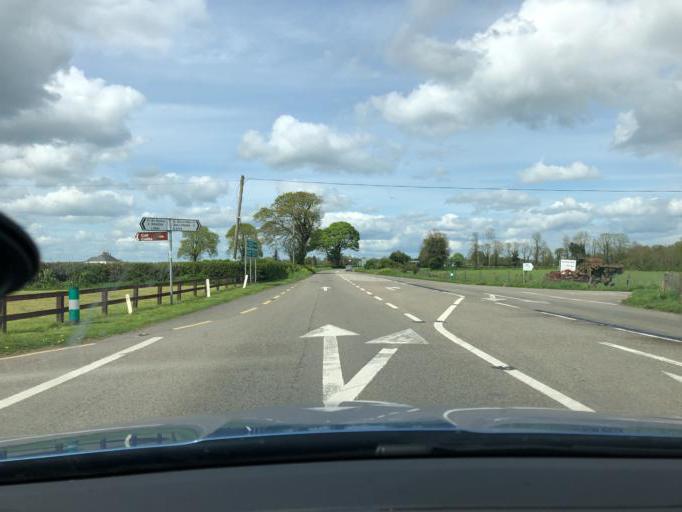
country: IE
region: Leinster
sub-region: Laois
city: Abbeyleix
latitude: 52.9601
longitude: -7.3439
